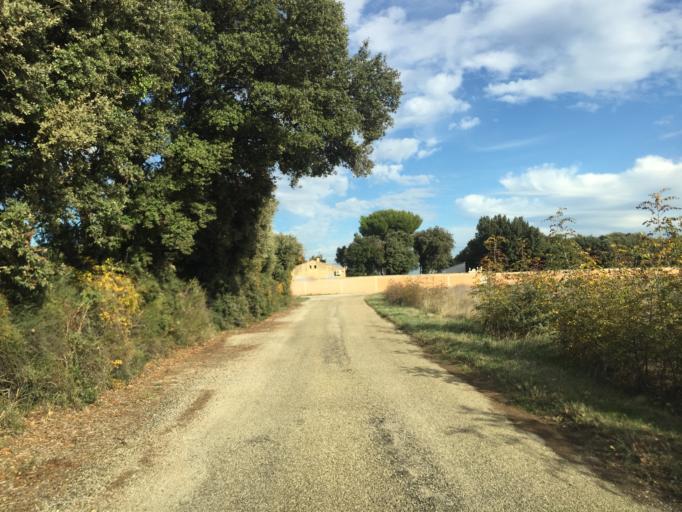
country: FR
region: Provence-Alpes-Cote d'Azur
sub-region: Departement du Vaucluse
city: Courthezon
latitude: 44.1071
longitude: 4.8745
